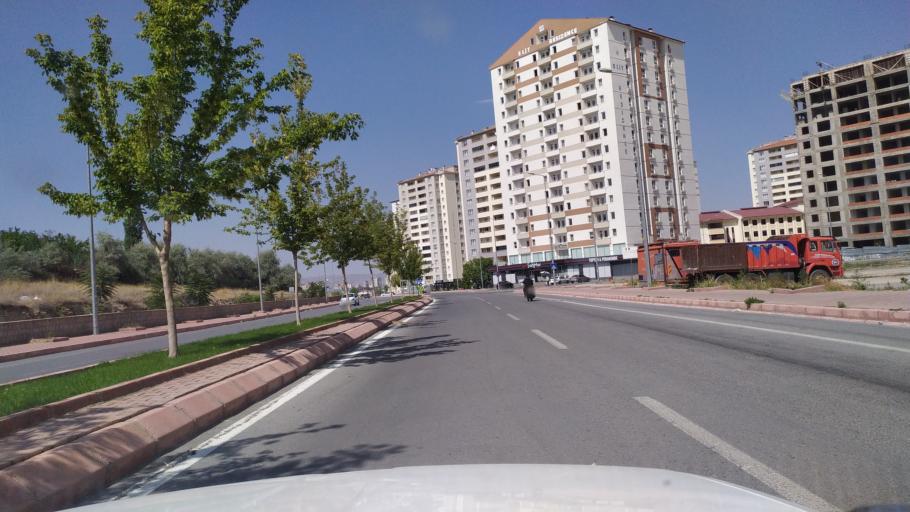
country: TR
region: Kayseri
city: Talas
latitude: 38.7146
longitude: 35.5563
